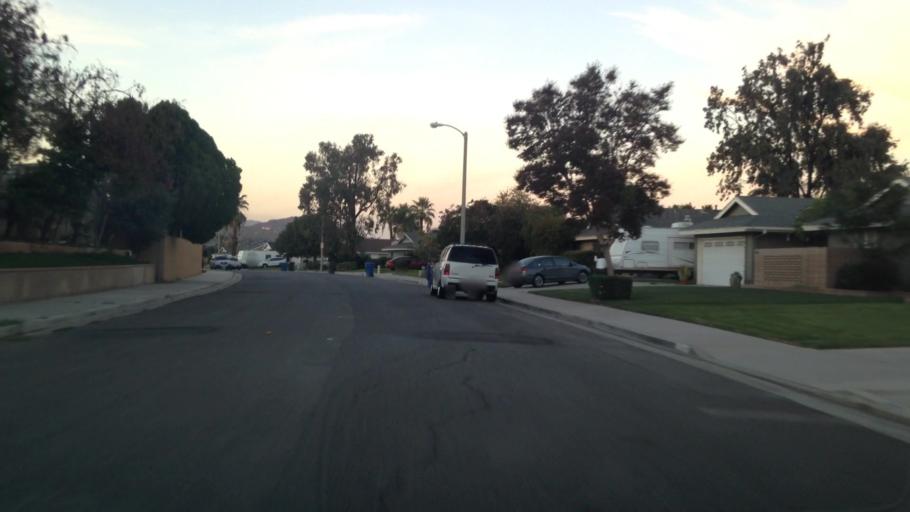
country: US
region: California
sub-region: Riverside County
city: Riverside
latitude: 33.9549
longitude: -117.4320
